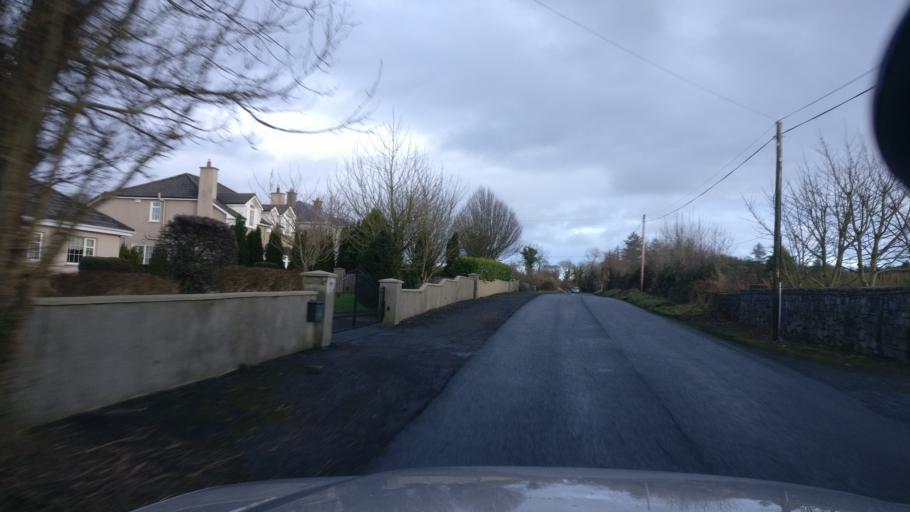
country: IE
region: Connaught
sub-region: County Galway
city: Athenry
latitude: 53.2967
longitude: -8.6717
